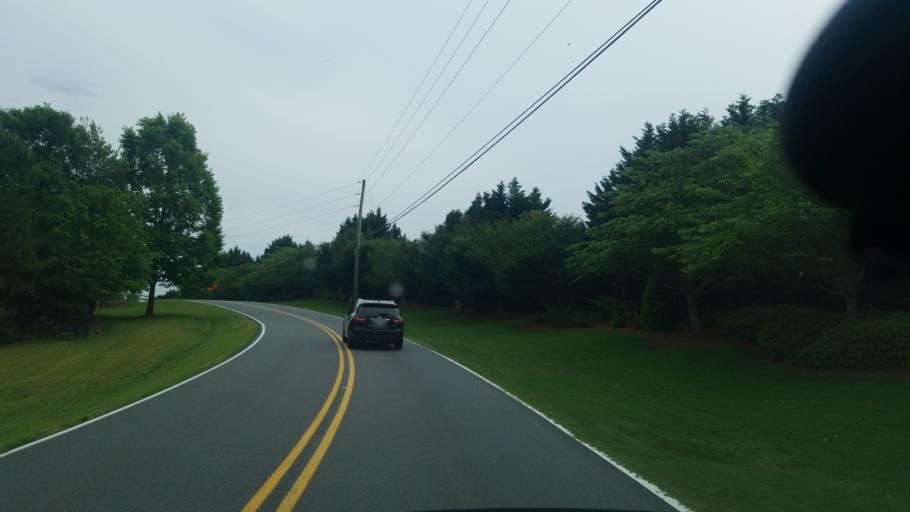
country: US
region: Georgia
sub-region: Forsyth County
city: Cumming
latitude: 34.1196
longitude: -84.1285
